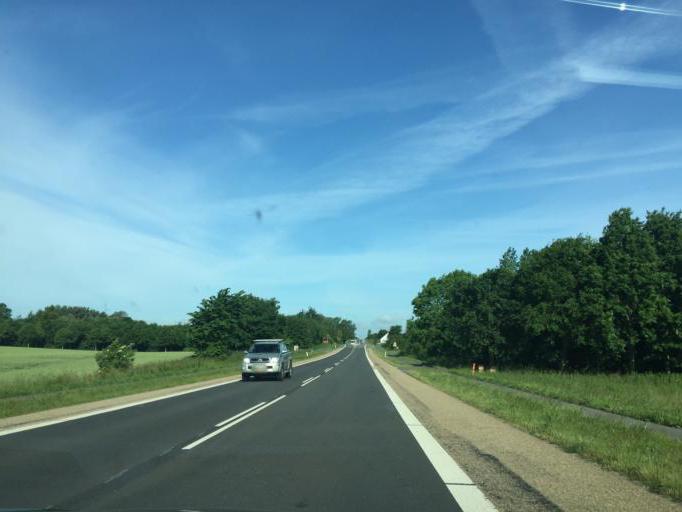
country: DK
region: South Denmark
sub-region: Middelfart Kommune
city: Norre Aby
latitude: 55.4776
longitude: 9.8575
